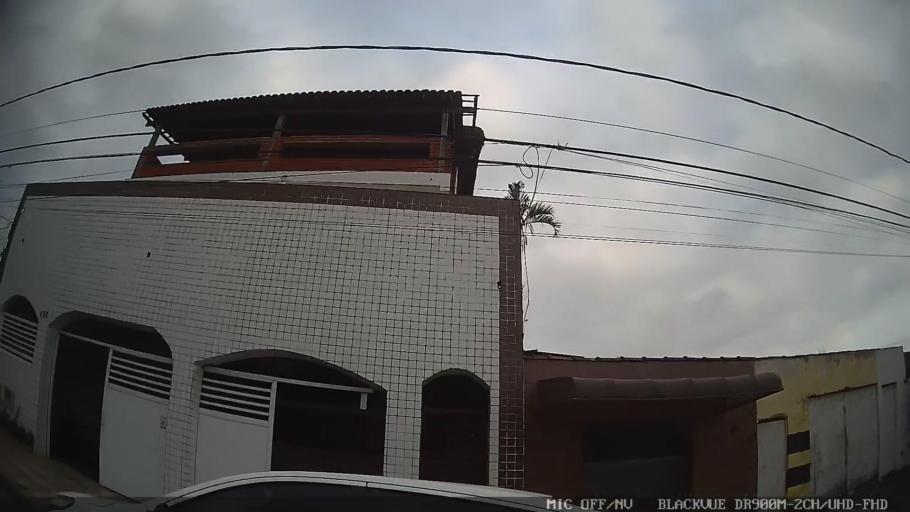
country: BR
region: Sao Paulo
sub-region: Santos
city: Santos
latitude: -23.9445
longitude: -46.3013
